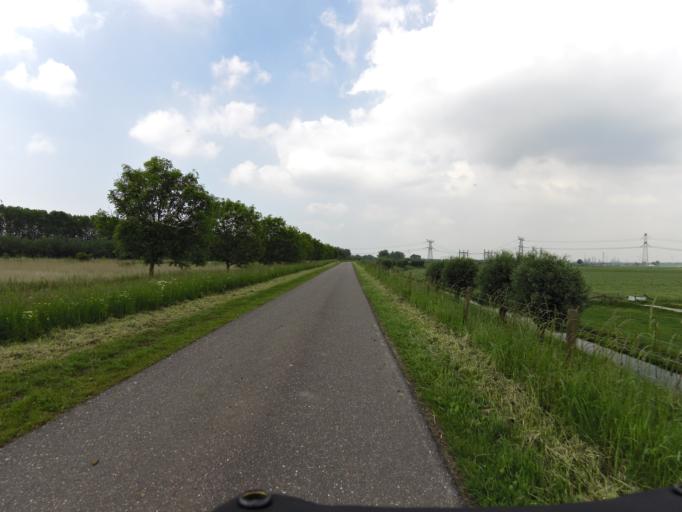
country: NL
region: South Holland
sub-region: Gemeente Spijkenisse
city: Spijkenisse
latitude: 51.8333
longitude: 4.2640
